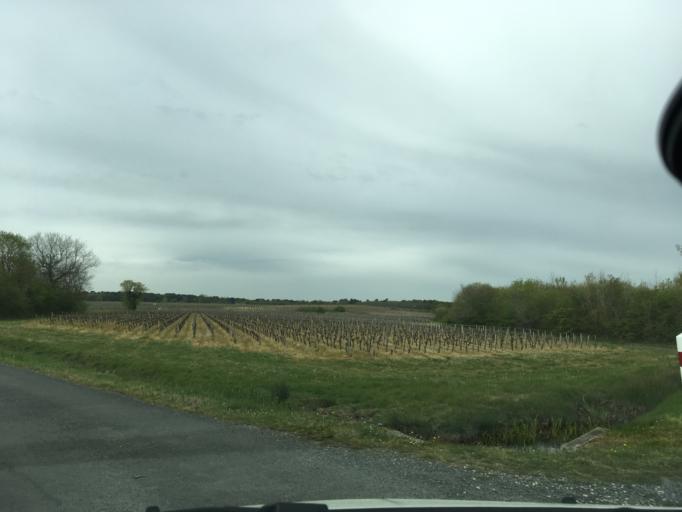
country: FR
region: Aquitaine
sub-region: Departement de la Gironde
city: Lesparre-Medoc
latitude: 45.3232
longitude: -0.8948
